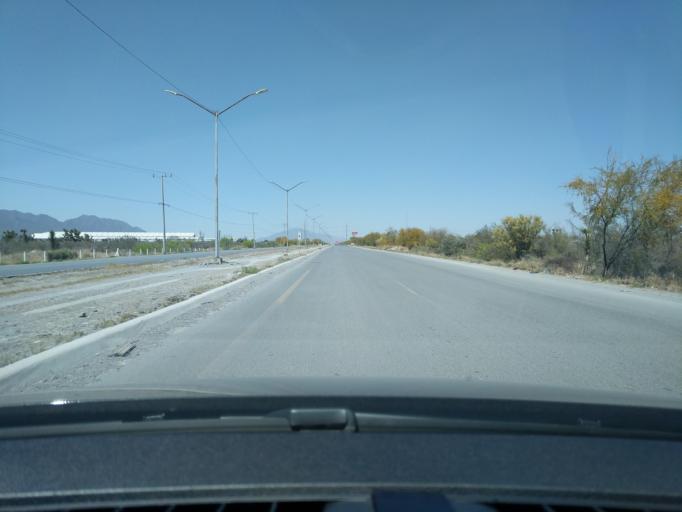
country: MX
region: Nuevo Leon
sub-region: Salinas Victoria
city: Emiliano Zapata
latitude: 25.9201
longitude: -100.2707
